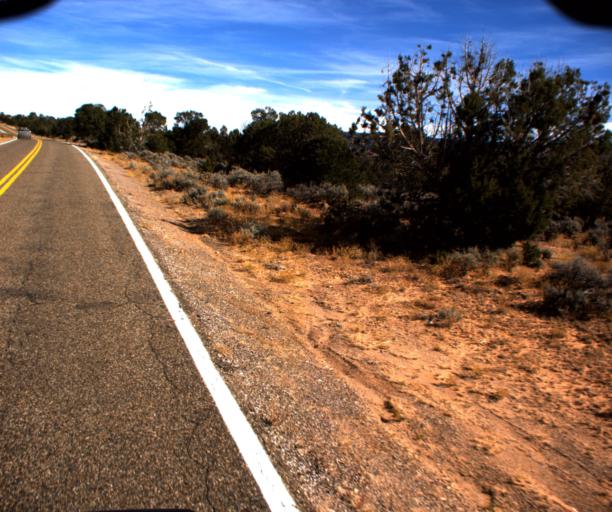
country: US
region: Arizona
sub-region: Navajo County
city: Kayenta
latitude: 36.5759
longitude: -110.4929
